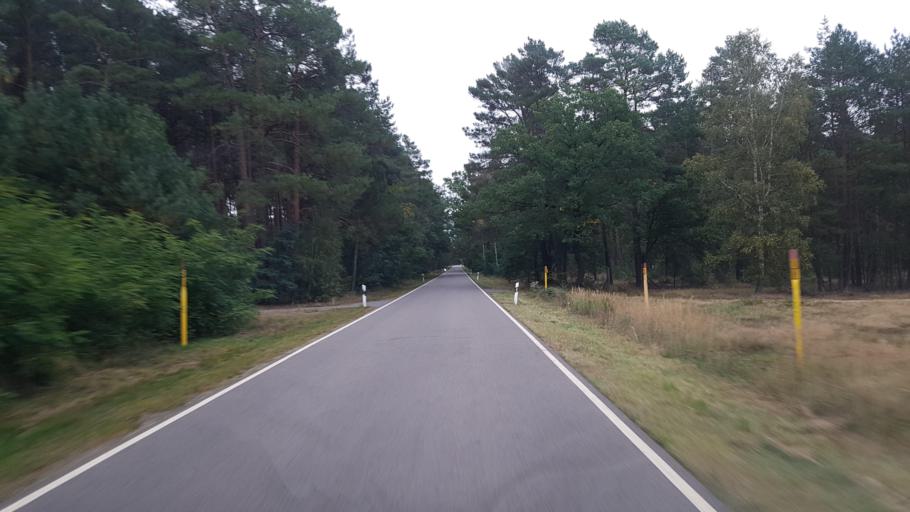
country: DE
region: Brandenburg
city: Luckau
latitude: 51.8811
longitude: 13.6777
